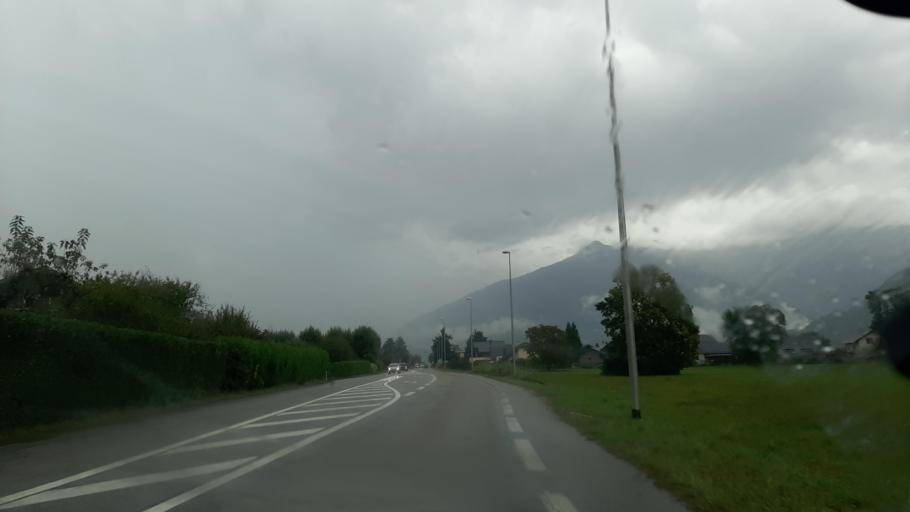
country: FR
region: Rhone-Alpes
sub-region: Departement de la Savoie
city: Gilly-sur-Isere
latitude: 45.6563
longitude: 6.3476
